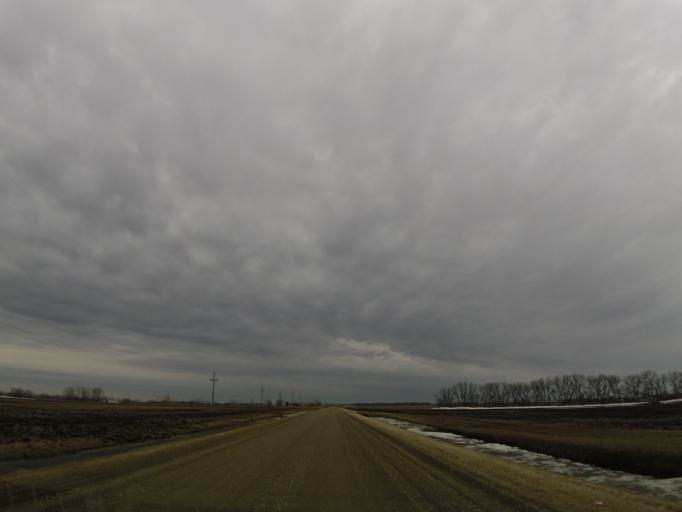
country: US
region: North Dakota
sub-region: Walsh County
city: Grafton
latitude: 48.4198
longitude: -97.4386
